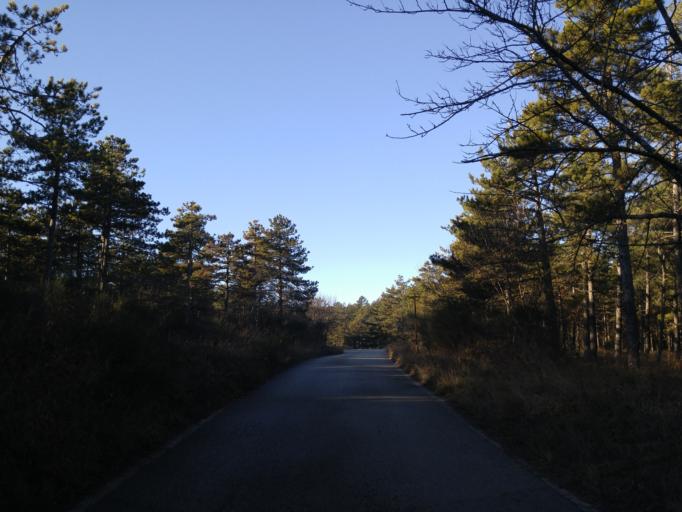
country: IT
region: The Marches
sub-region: Provincia di Pesaro e Urbino
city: Isola del Piano
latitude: 43.7056
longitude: 12.7581
